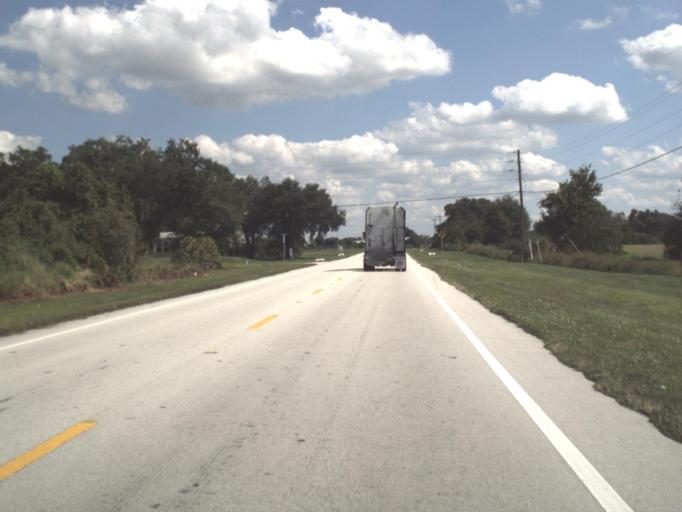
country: US
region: Florida
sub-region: Hardee County
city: Zolfo Springs
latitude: 27.4929
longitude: -81.7775
